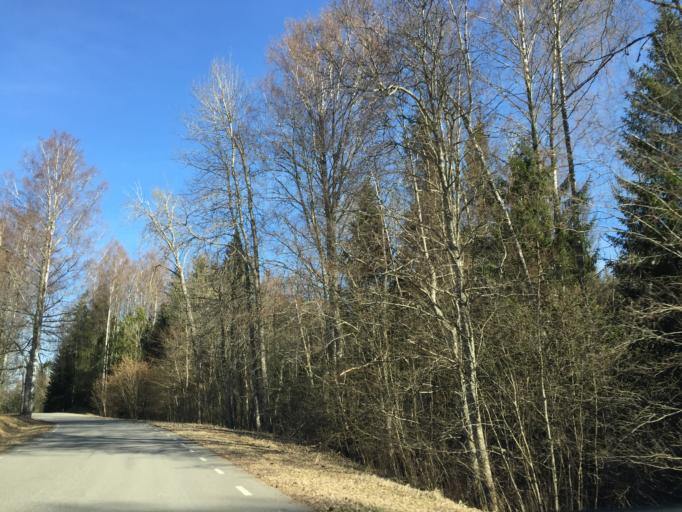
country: EE
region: Vorumaa
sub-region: Antsla vald
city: Vana-Antsla
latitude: 58.0171
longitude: 26.4595
